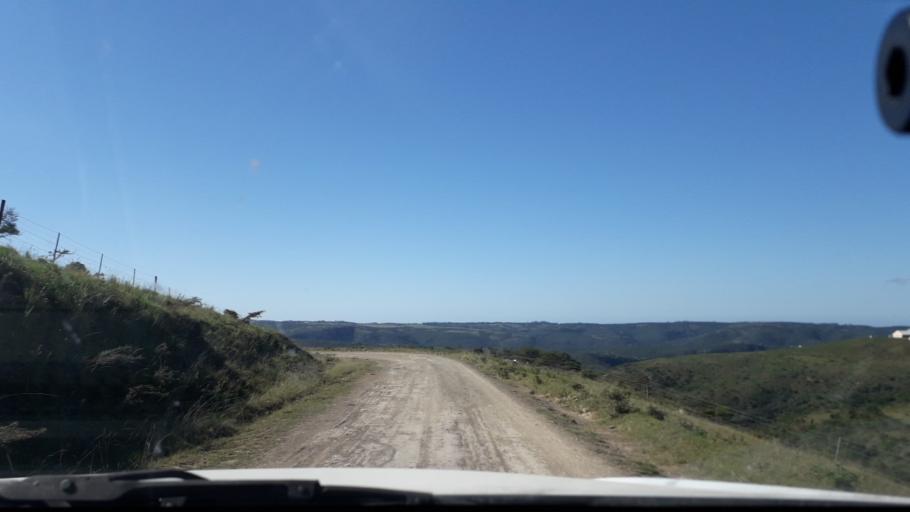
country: ZA
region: Eastern Cape
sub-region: Amathole District Municipality
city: Komga
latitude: -32.7879
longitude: 27.9529
